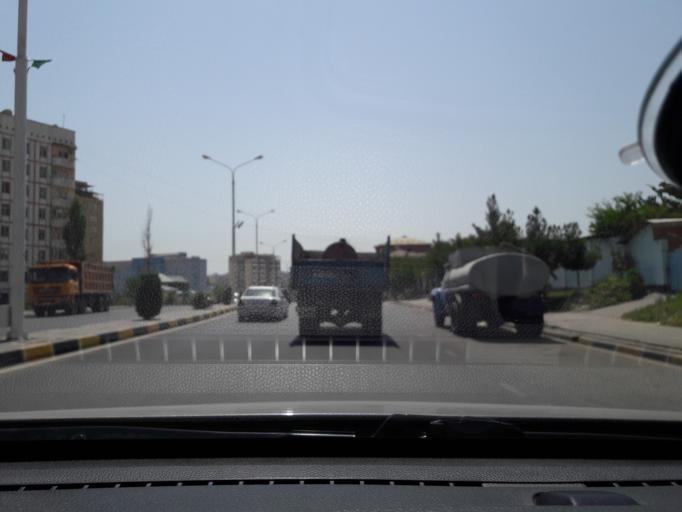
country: TJ
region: Dushanbe
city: Dushanbe
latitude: 38.5876
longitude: 68.7159
